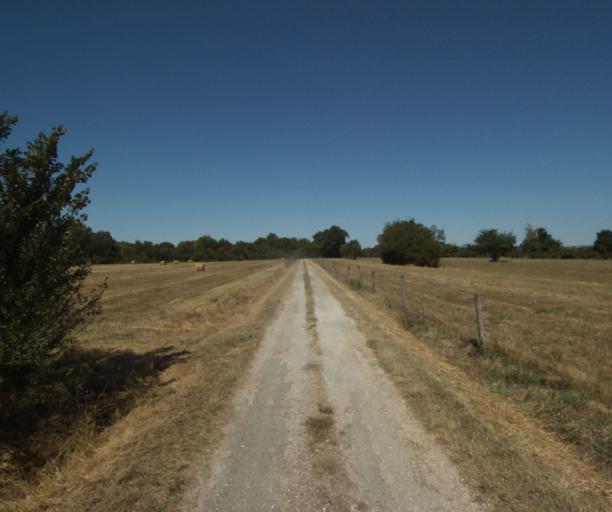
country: FR
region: Midi-Pyrenees
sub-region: Departement de la Haute-Garonne
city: Revel
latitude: 43.4695
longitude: 1.9858
